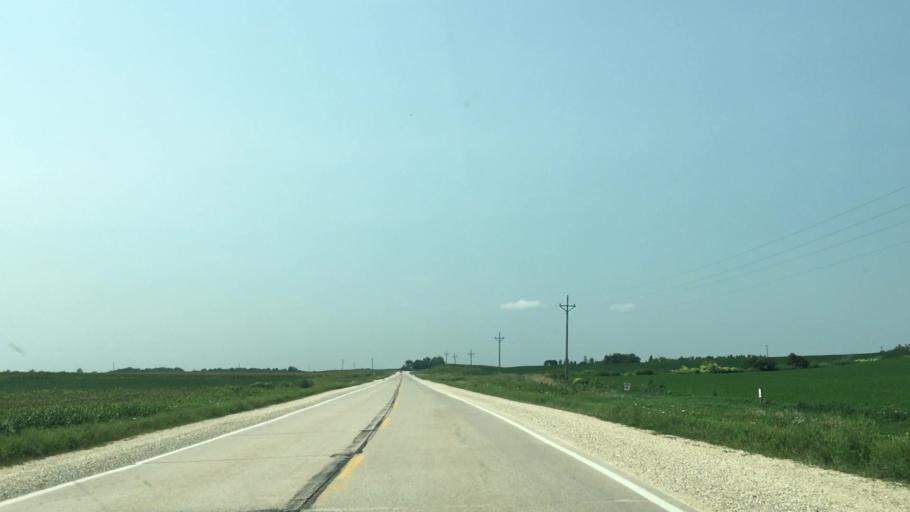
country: US
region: Iowa
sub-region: Fayette County
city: West Union
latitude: 43.0936
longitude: -91.8580
